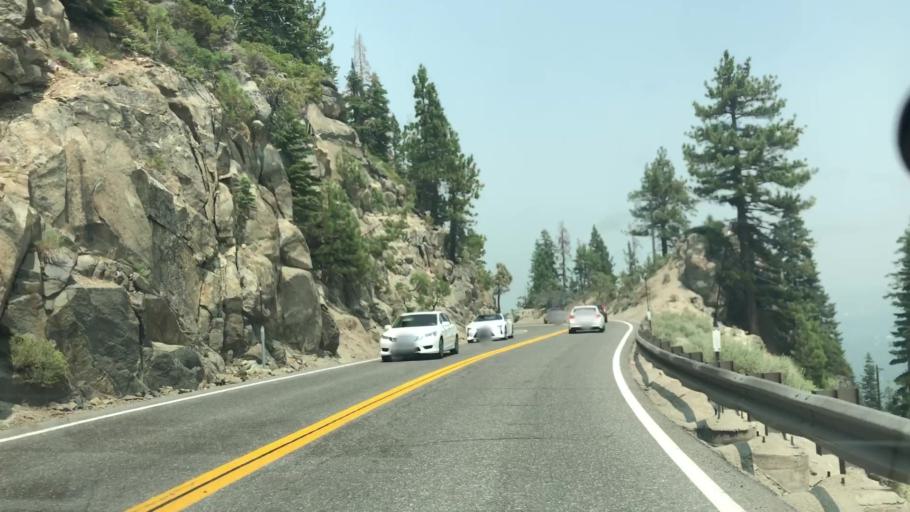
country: US
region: California
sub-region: El Dorado County
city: South Lake Tahoe
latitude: 38.8240
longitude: -120.0283
